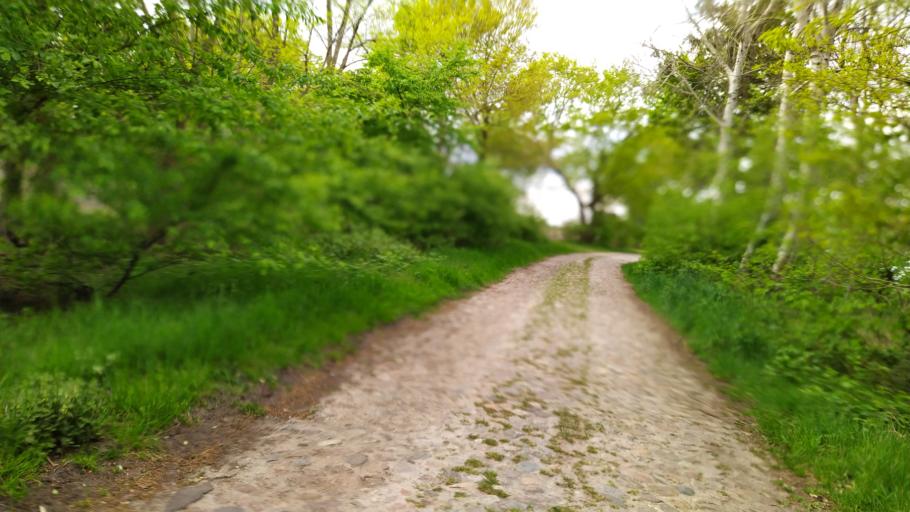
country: DE
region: Lower Saxony
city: Farven
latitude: 53.4323
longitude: 9.3315
